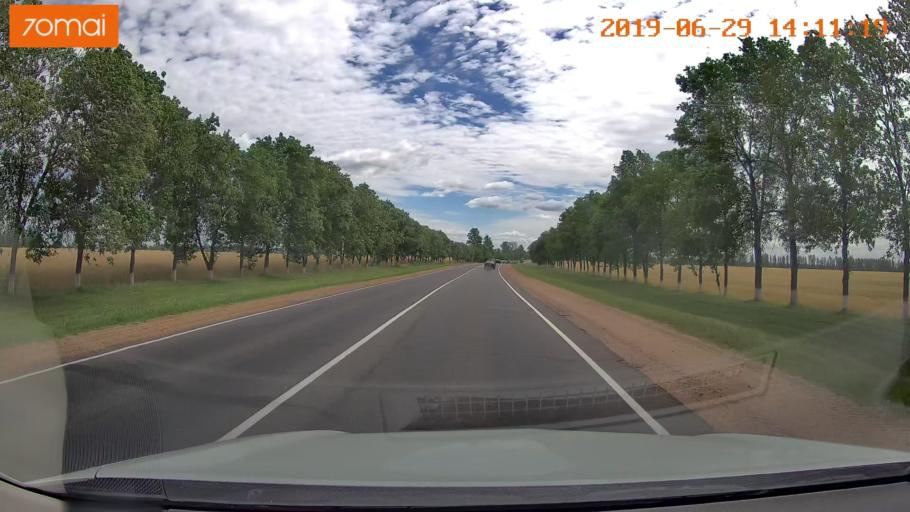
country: BY
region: Minsk
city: Salihorsk
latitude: 52.8210
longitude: 27.5020
